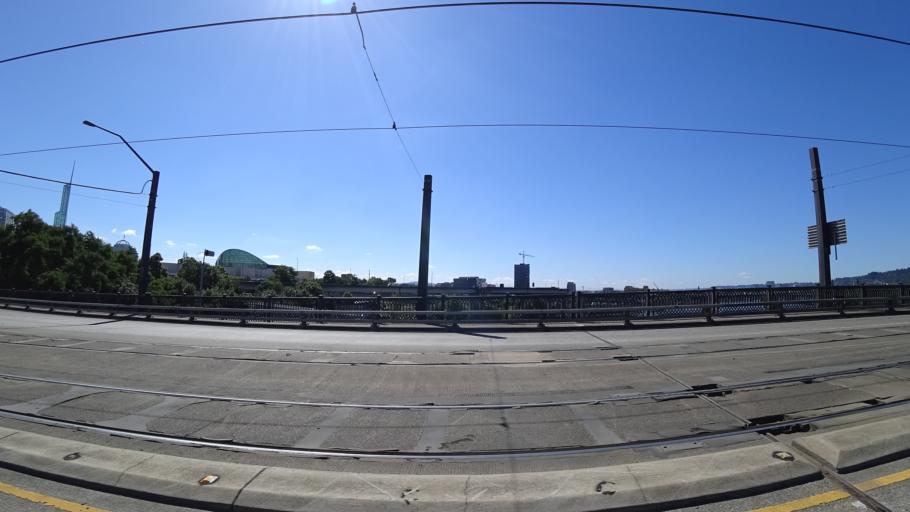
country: US
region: Oregon
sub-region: Multnomah County
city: Portland
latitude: 45.5283
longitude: -122.6683
